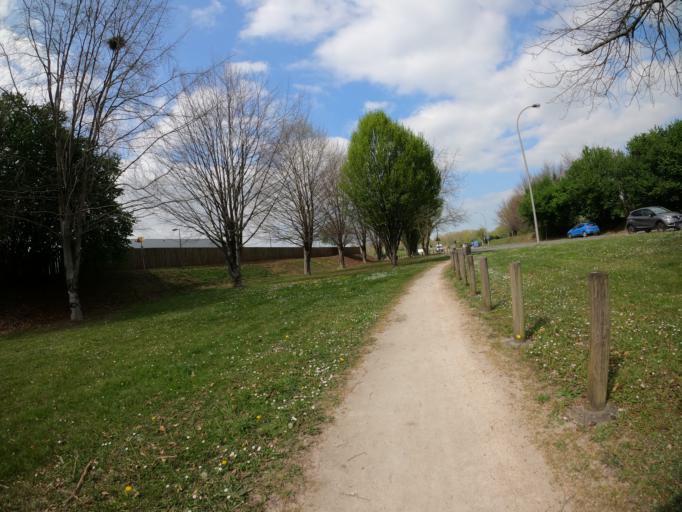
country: FR
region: Aquitaine
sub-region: Departement des Pyrenees-Atlantiques
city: Lons
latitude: 43.3385
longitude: -0.3854
